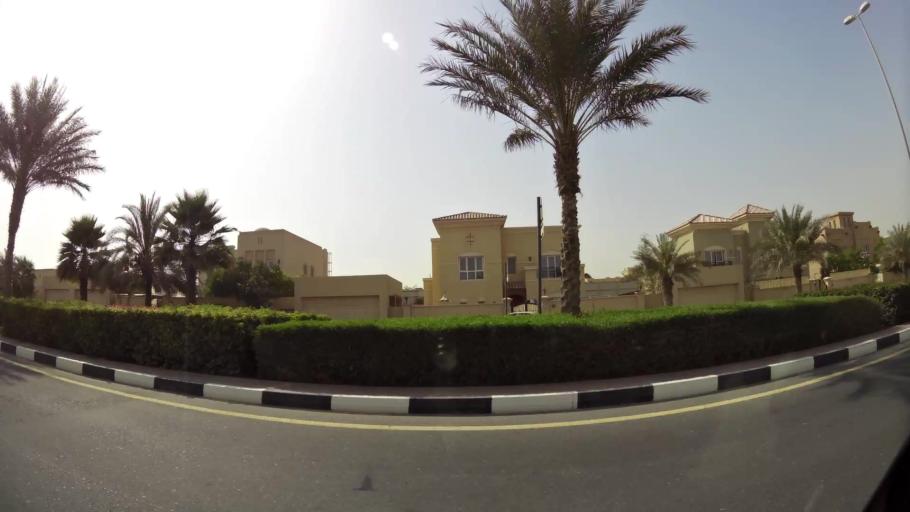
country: AE
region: Ash Shariqah
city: Sharjah
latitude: 25.2654
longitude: 55.4473
